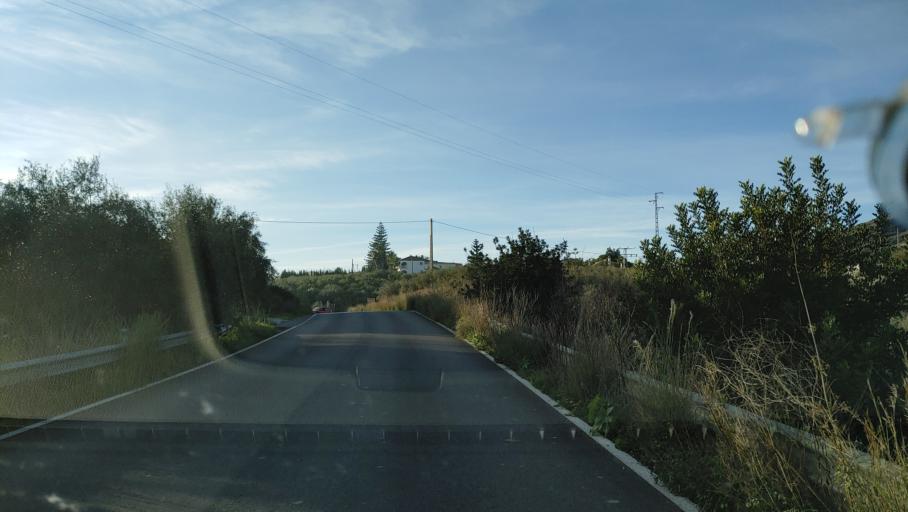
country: ES
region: Andalusia
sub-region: Provincia de Malaga
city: Cartama
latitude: 36.6821
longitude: -4.6336
